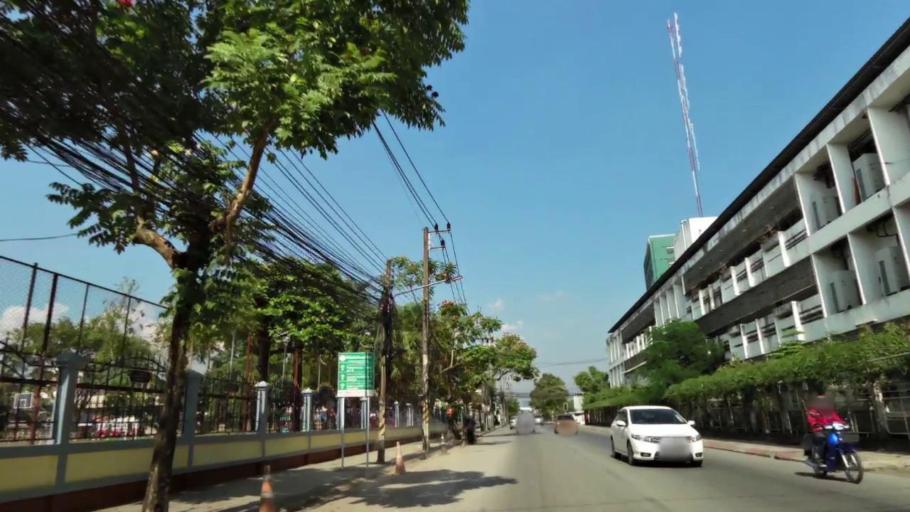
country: TH
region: Chiang Rai
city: Chiang Rai
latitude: 19.9012
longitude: 99.8281
